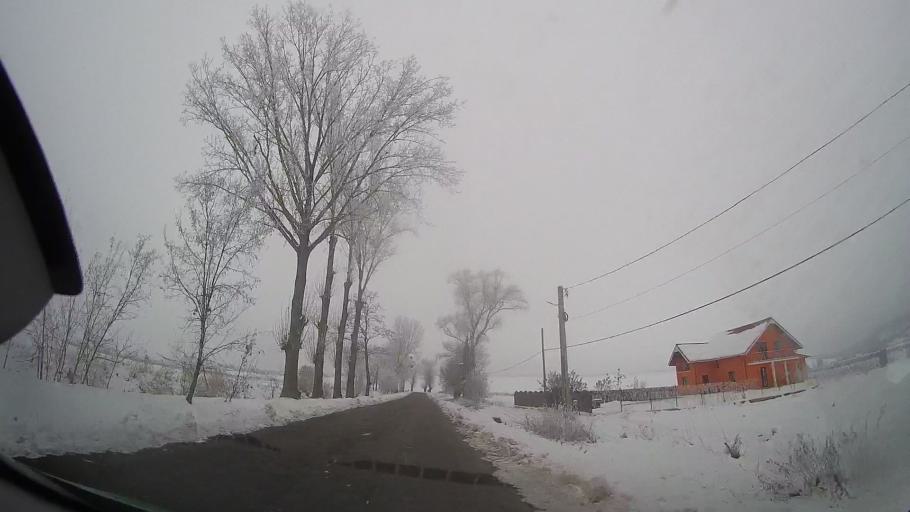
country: RO
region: Neamt
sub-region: Comuna Valea Ursului
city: Chilii
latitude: 46.8522
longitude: 27.0391
